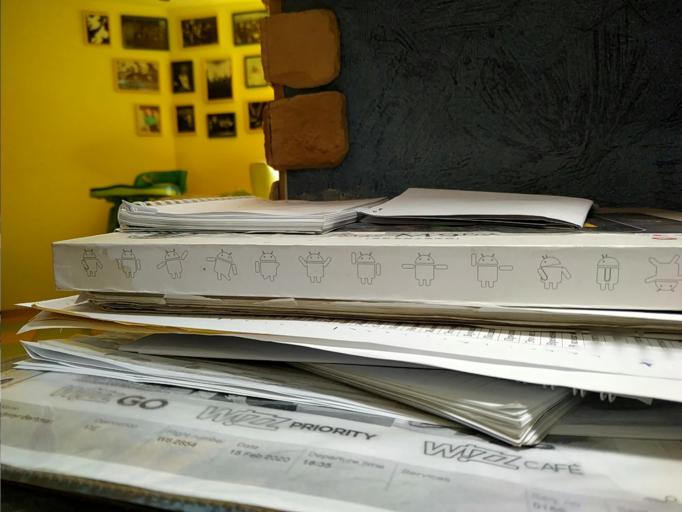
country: RU
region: Novgorod
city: Utorgosh
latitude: 58.1191
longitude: 30.0841
